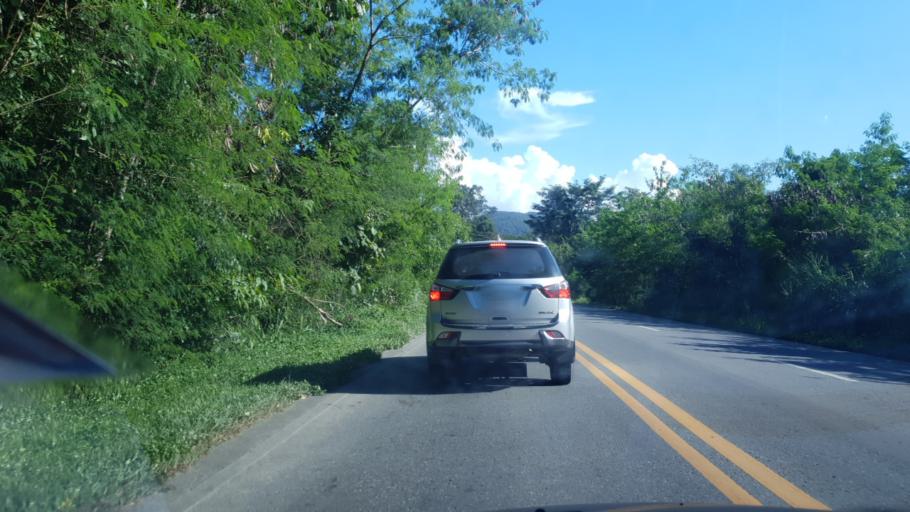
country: TH
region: Chiang Mai
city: Mae On
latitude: 18.9252
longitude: 99.2393
